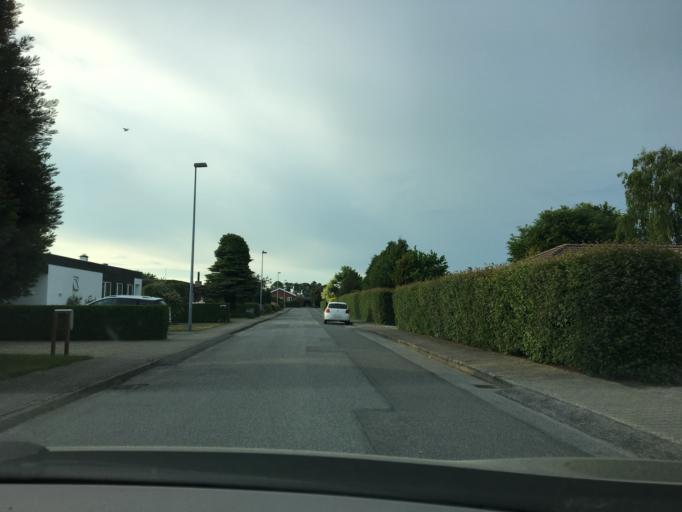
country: DK
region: South Denmark
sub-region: Fredericia Kommune
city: Fredericia
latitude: 55.5796
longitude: 9.7789
